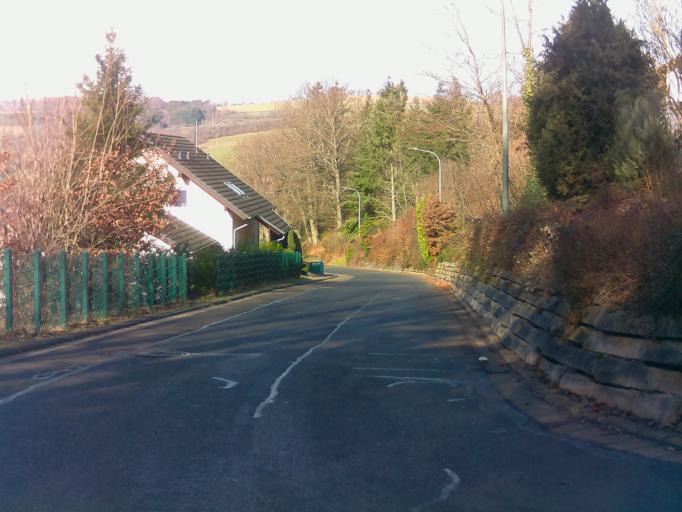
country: DE
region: Rheinland-Pfalz
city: Herschweiler-Pettersheim
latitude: 49.4754
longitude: 7.3513
